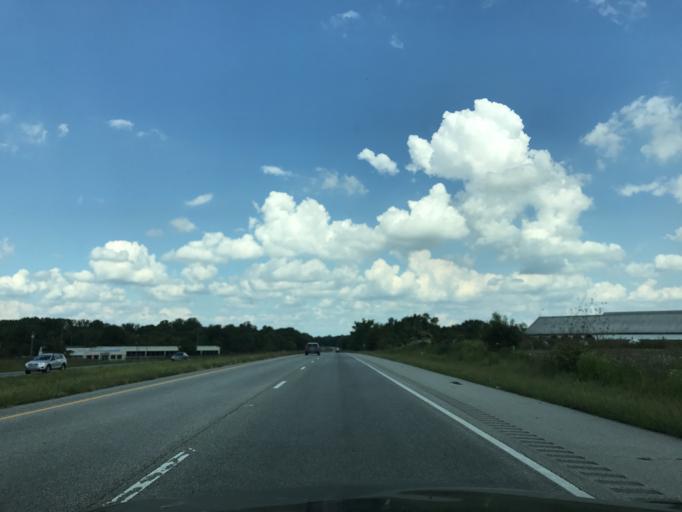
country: US
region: Maryland
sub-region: Queen Anne's County
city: Kingstown
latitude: 39.2469
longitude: -75.8709
